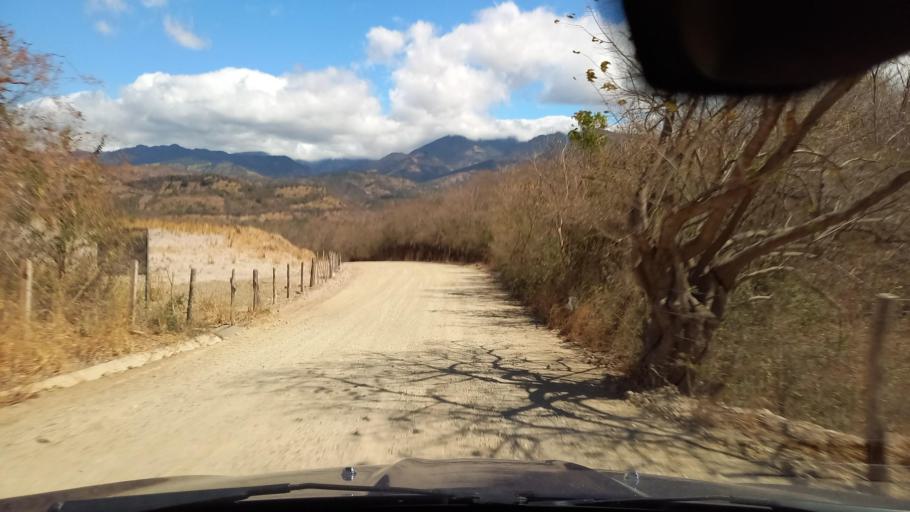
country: SV
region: Santa Ana
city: Metapan
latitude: 14.3566
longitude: -89.4788
